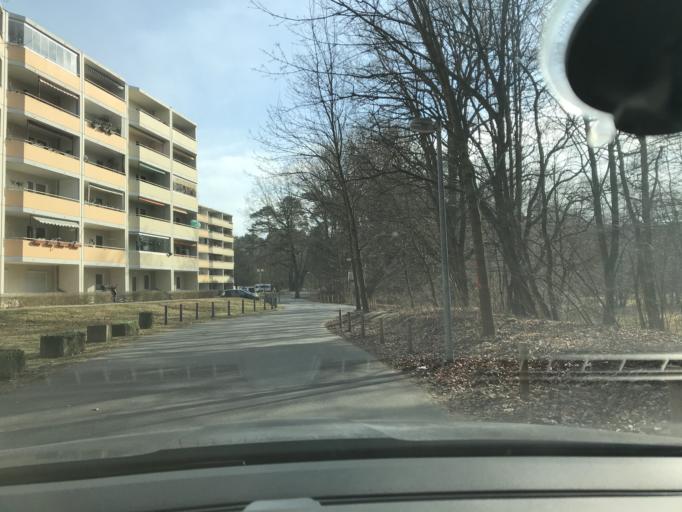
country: DE
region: Brandenburg
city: Erkner
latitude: 52.4141
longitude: 13.7605
